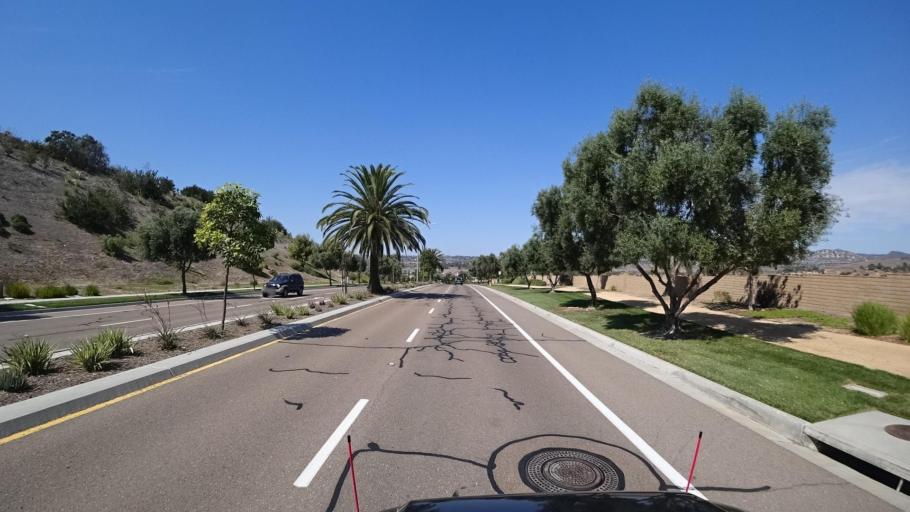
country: US
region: California
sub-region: San Diego County
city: La Presa
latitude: 32.6717
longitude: -116.9877
